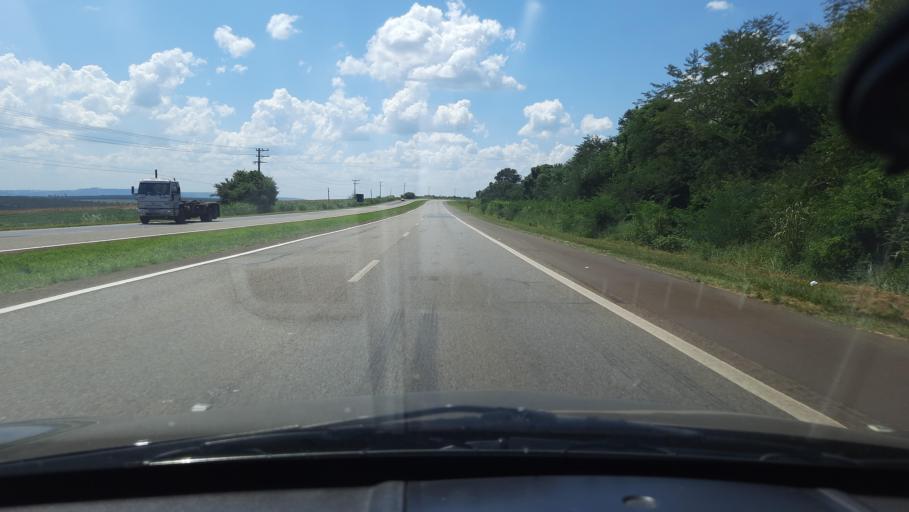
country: BR
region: Sao Paulo
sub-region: Casa Branca
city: Casa Branca
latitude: -21.7132
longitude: -47.0836
